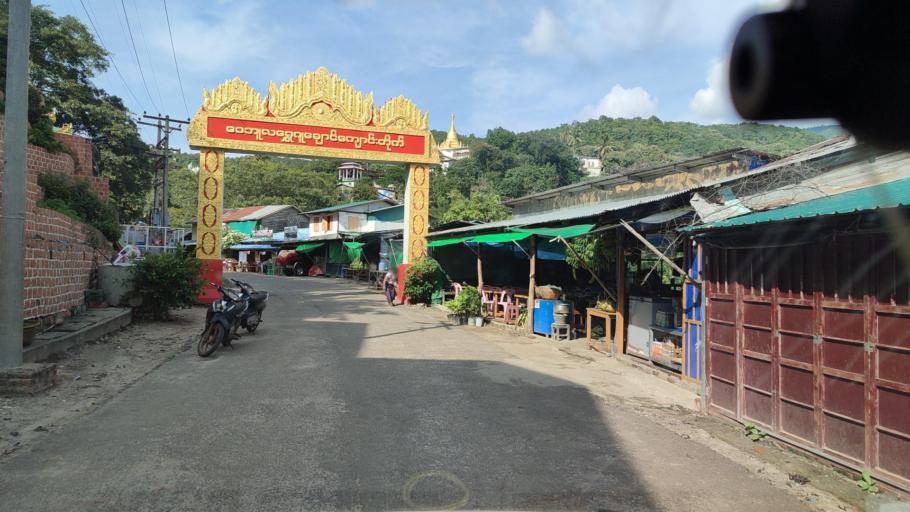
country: MM
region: Magway
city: Chauk
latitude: 20.9127
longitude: 95.2106
